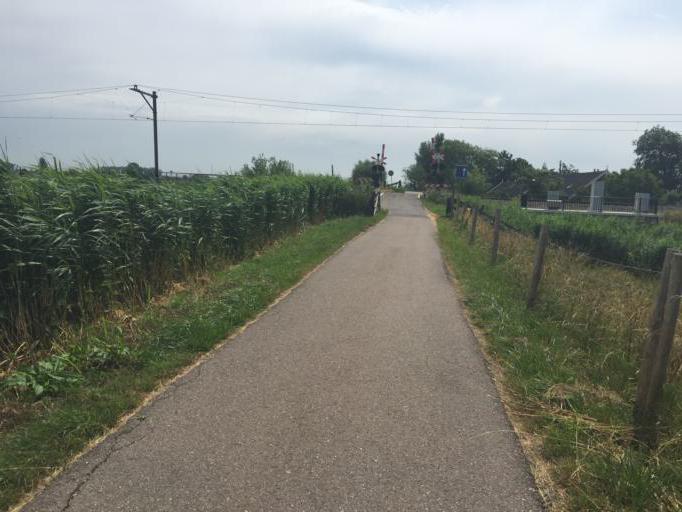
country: NL
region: South Holland
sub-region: Bodegraven-Reeuwijk
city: Bodegraven
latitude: 52.0764
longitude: 4.7863
